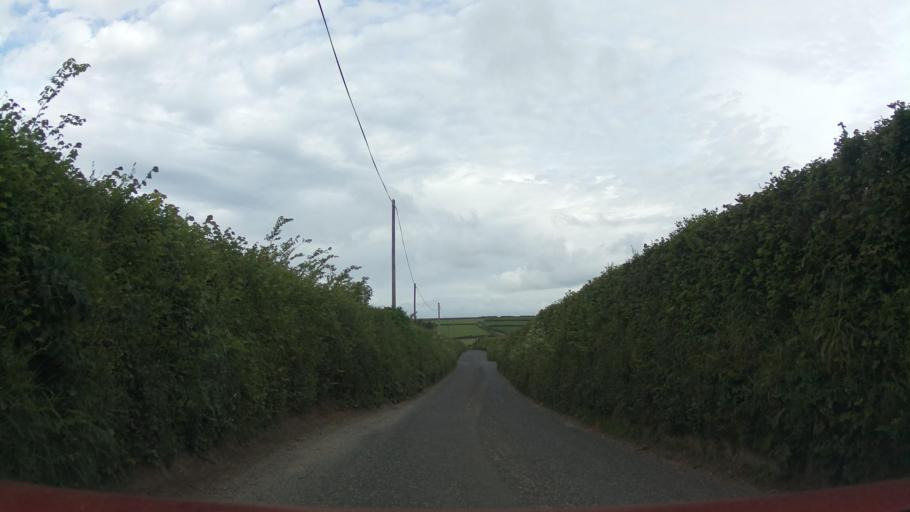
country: GB
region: England
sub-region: Devon
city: Dartmouth
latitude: 50.3192
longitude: -3.6351
